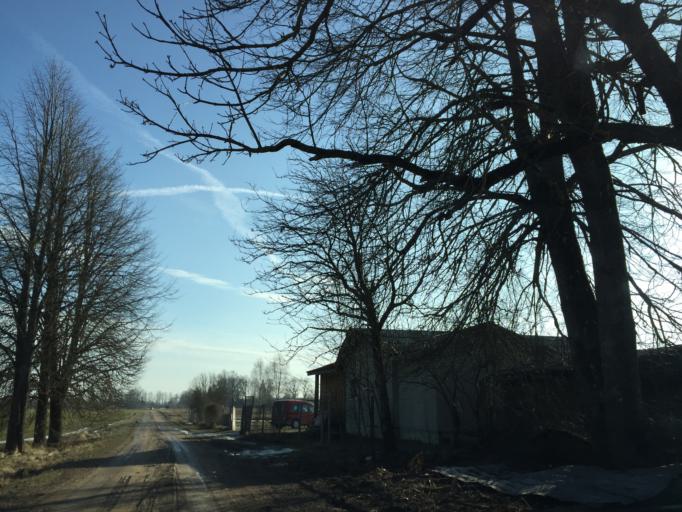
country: LV
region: Lecava
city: Iecava
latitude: 56.6807
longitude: 24.2051
